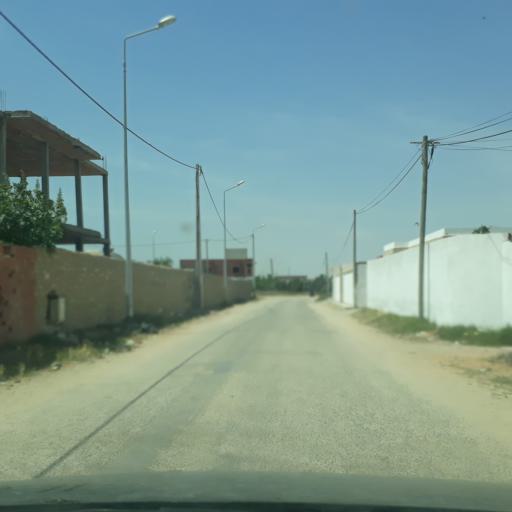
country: TN
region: Safaqis
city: Al Qarmadah
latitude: 34.8269
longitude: 10.7790
